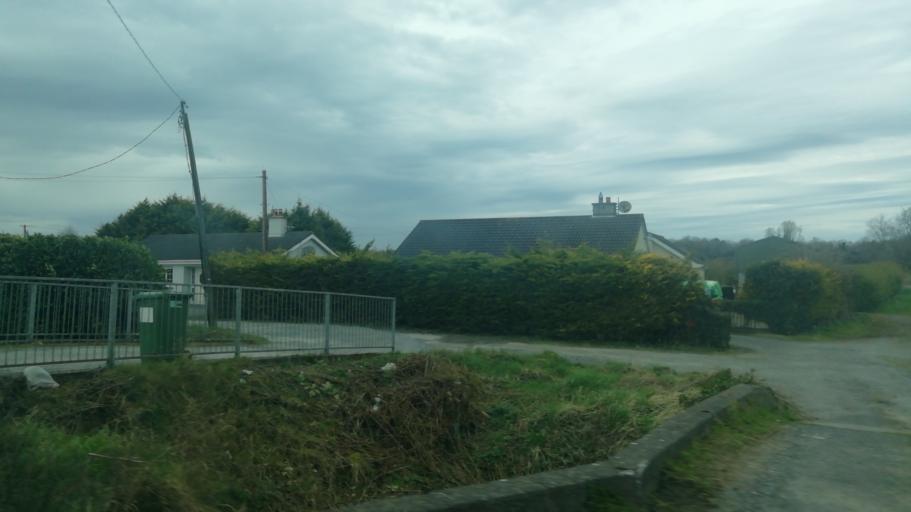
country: IE
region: Leinster
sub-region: Kildare
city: Derrinturn
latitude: 53.2824
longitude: -6.9001
